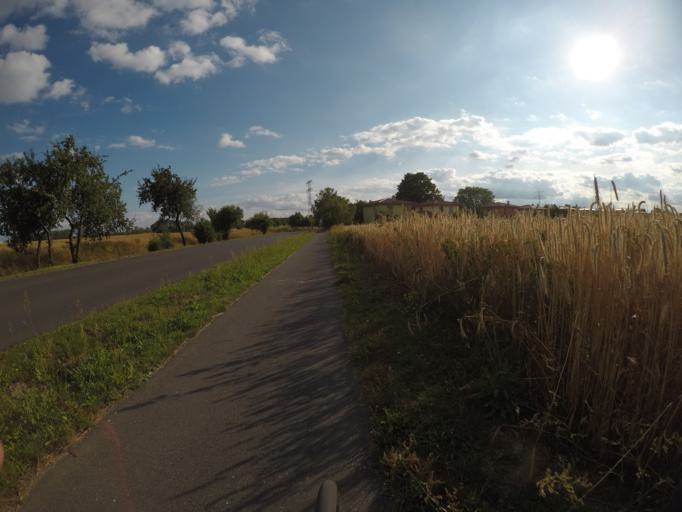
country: DE
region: Berlin
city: Falkenberg
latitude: 52.5908
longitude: 13.5441
